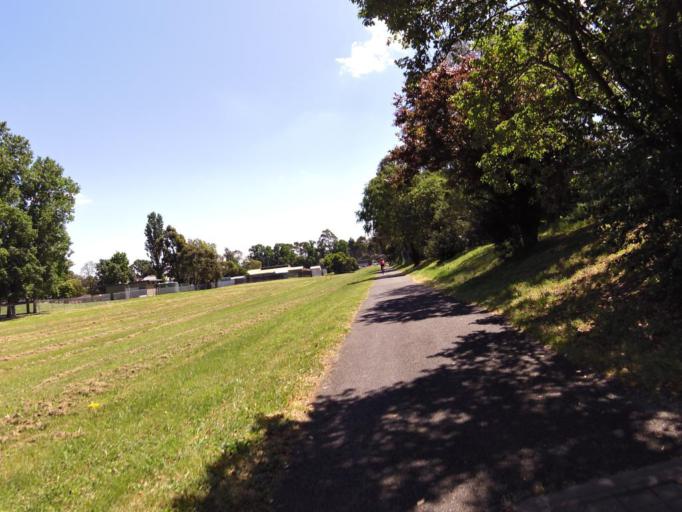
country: AU
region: Victoria
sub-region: Knox
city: Ferntree Gully
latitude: -37.8906
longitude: 145.2985
